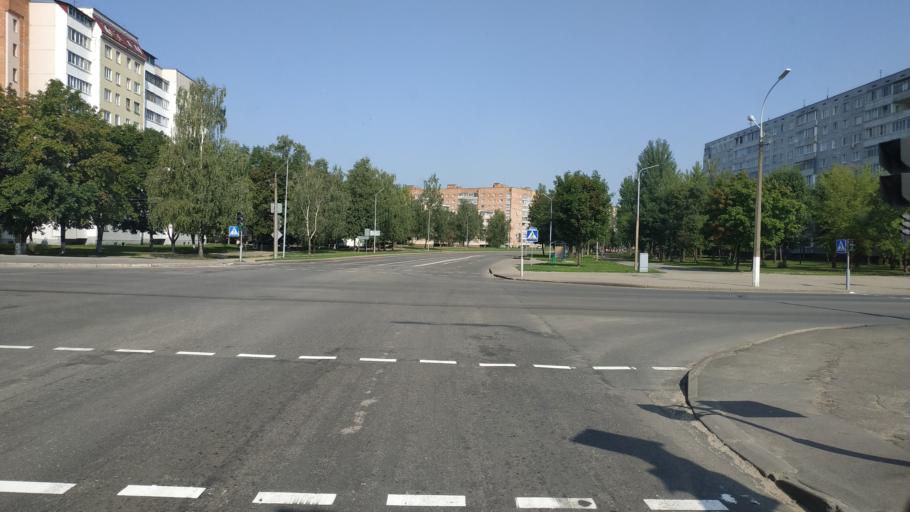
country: BY
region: Mogilev
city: Buynichy
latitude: 53.8662
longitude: 30.3159
